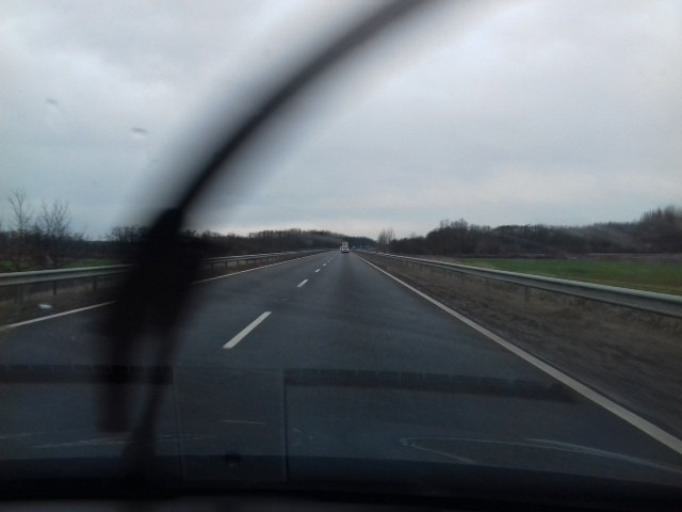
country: HU
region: Szabolcs-Szatmar-Bereg
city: Napkor
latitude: 47.9311
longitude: 21.8192
